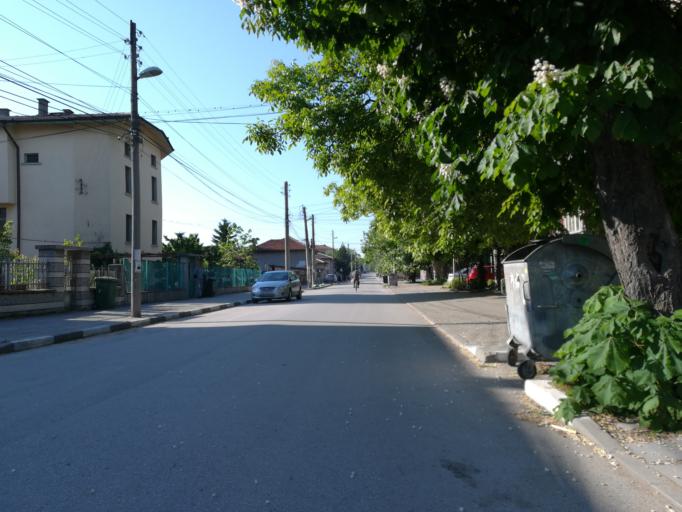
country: BG
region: Stara Zagora
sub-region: Obshtina Chirpan
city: Chirpan
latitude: 42.1049
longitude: 25.2248
